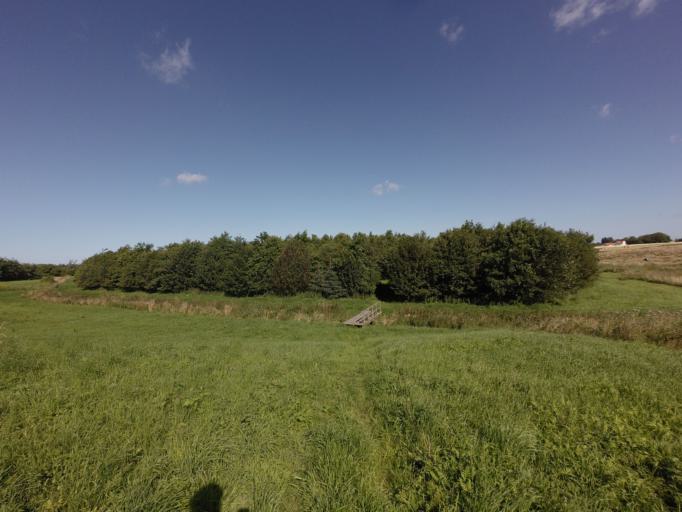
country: DK
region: North Denmark
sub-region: Hjorring Kommune
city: Vra
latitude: 57.3991
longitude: 9.7987
